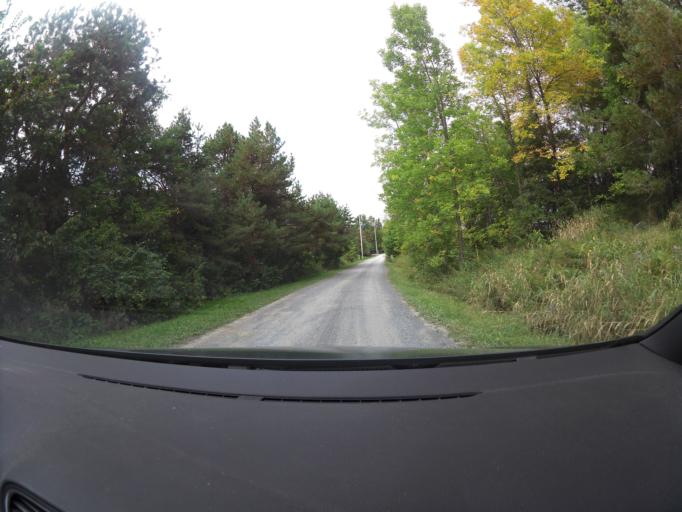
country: CA
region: Ontario
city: Arnprior
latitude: 45.3887
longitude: -76.2537
